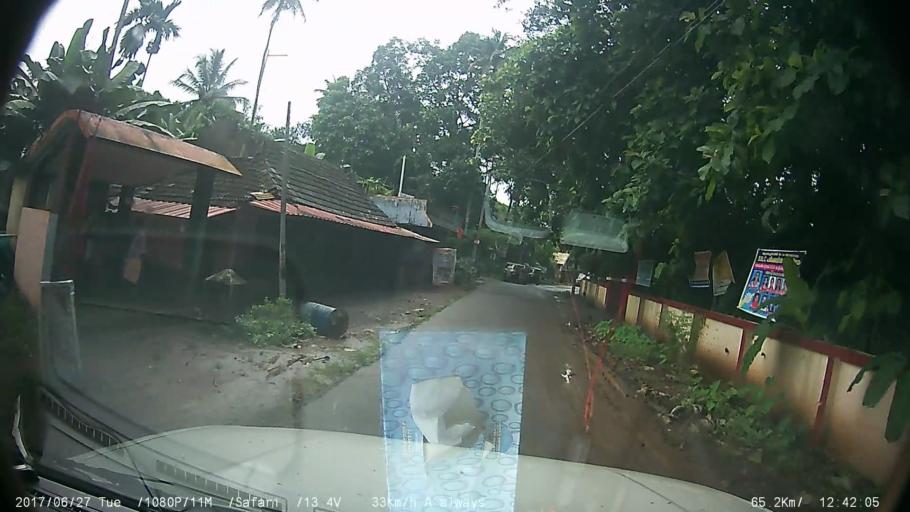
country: IN
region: Kerala
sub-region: Ernakulam
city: Piravam
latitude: 9.7825
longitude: 76.5333
